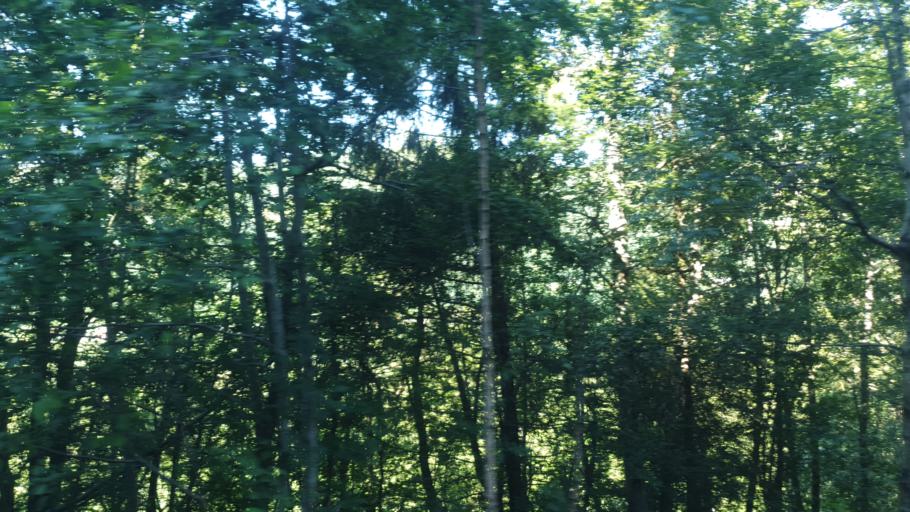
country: NO
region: Sor-Trondelag
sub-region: Meldal
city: Meldal
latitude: 63.1594
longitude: 9.7280
